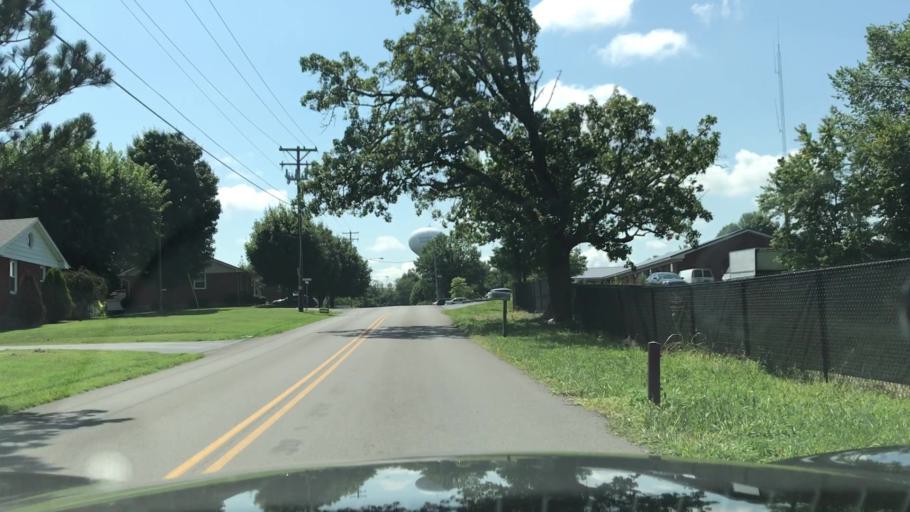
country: US
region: Kentucky
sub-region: Adair County
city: Columbia
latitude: 37.0962
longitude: -85.3120
